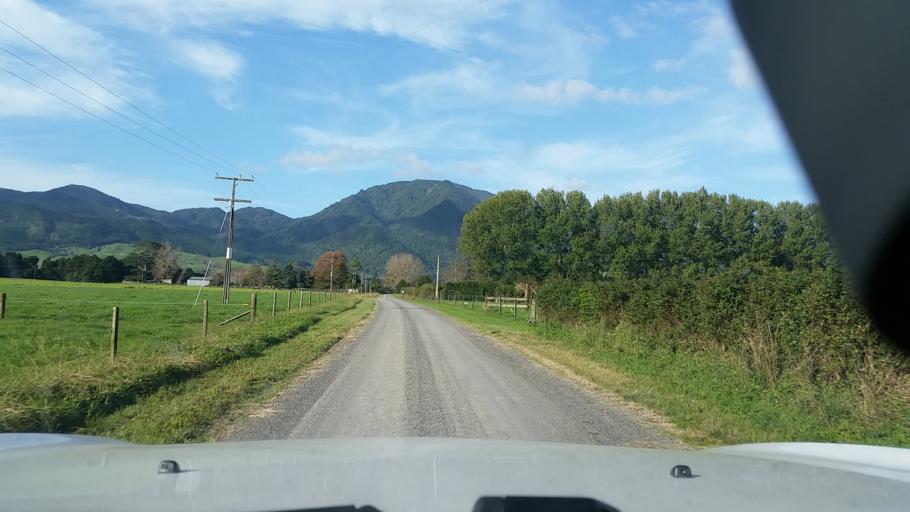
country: NZ
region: Waikato
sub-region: Matamata-Piako District
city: Matamata
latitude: -37.6588
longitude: 175.7901
